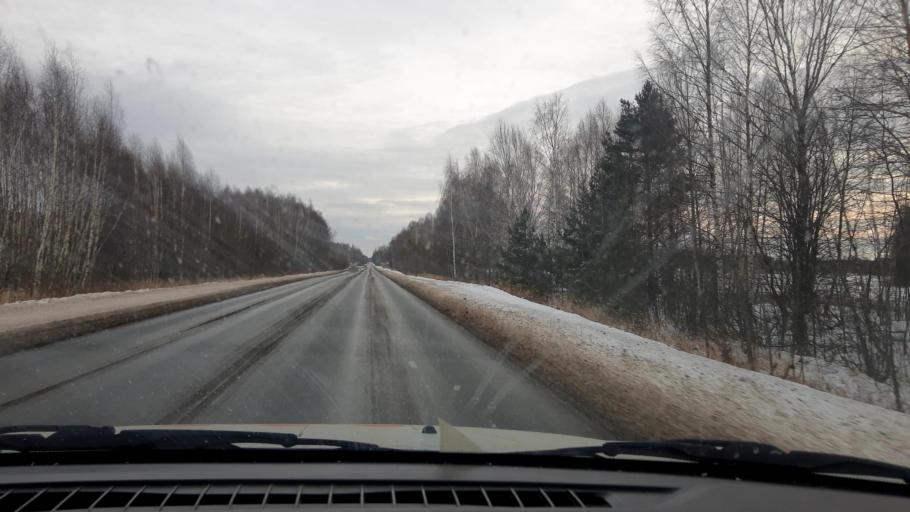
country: RU
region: Nizjnij Novgorod
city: Novaya Balakhna
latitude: 56.5722
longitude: 43.7072
